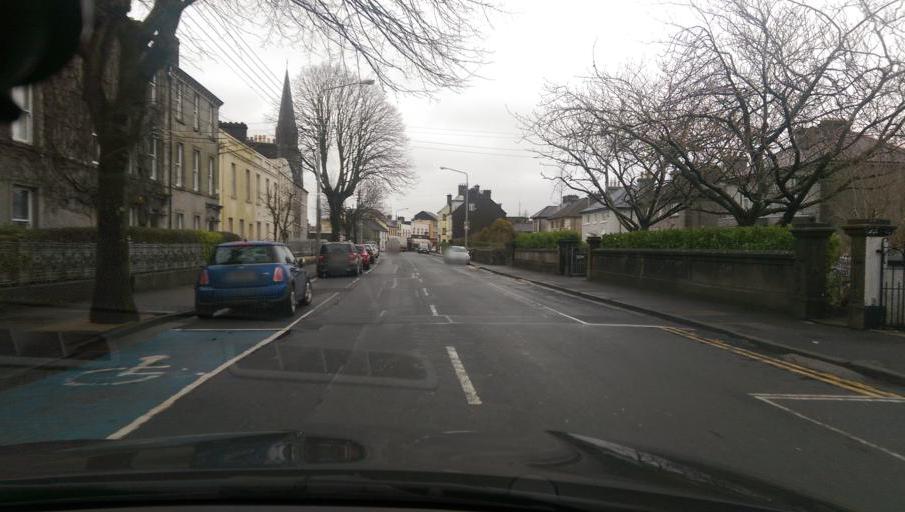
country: IE
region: Connaught
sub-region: County Galway
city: Gaillimh
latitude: 53.2686
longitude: -9.0623
